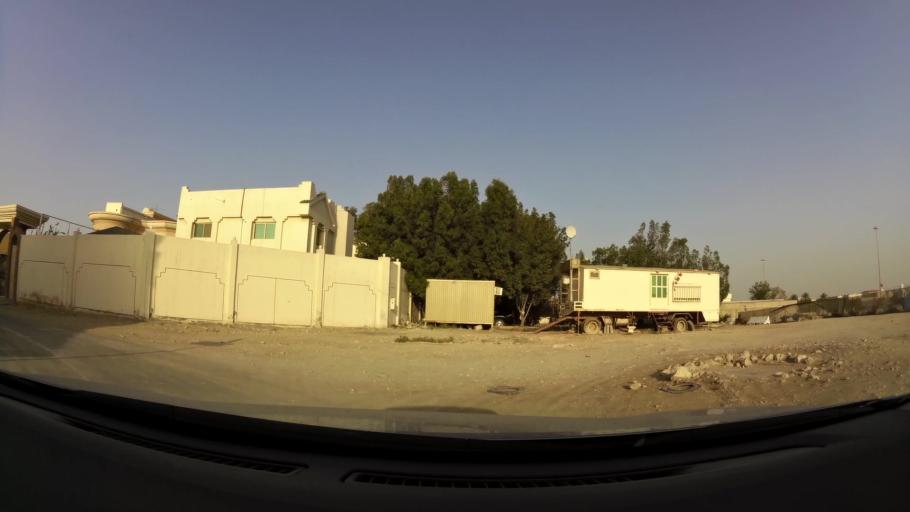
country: QA
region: Baladiyat ar Rayyan
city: Ar Rayyan
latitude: 25.3211
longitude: 51.4541
